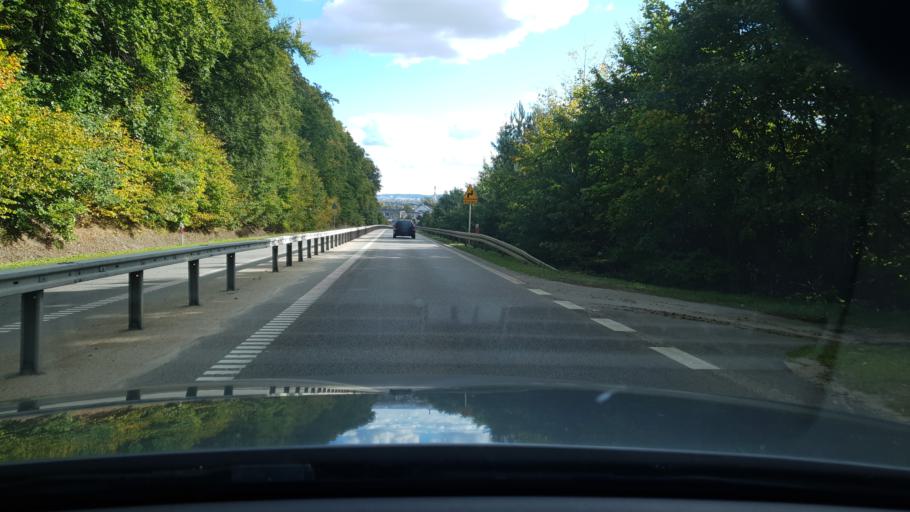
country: PL
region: Pomeranian Voivodeship
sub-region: Powiat wejherowski
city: Reda
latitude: 54.6213
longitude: 18.3391
